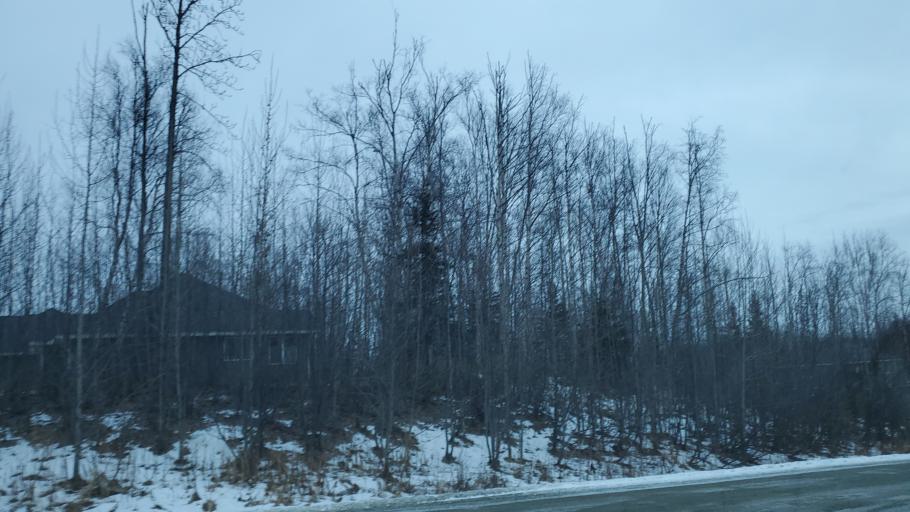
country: US
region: Alaska
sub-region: Matanuska-Susitna Borough
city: Farm Loop
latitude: 61.6566
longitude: -149.2230
